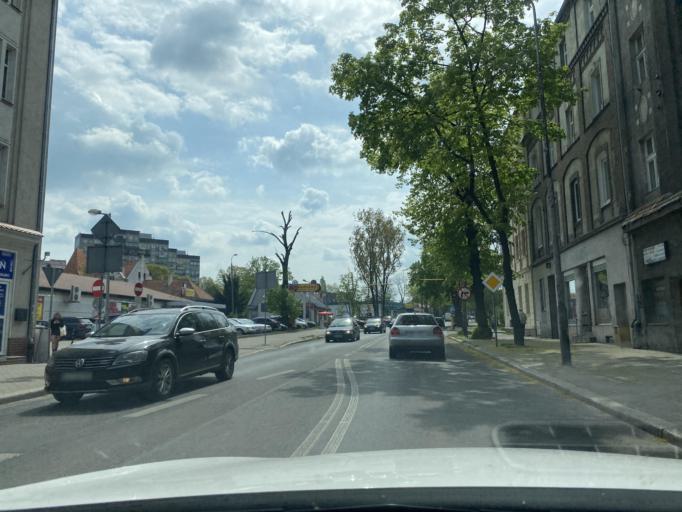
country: PL
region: Lower Silesian Voivodeship
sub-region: Powiat boleslawiecki
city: Boleslawiec
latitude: 51.2635
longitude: 15.5743
